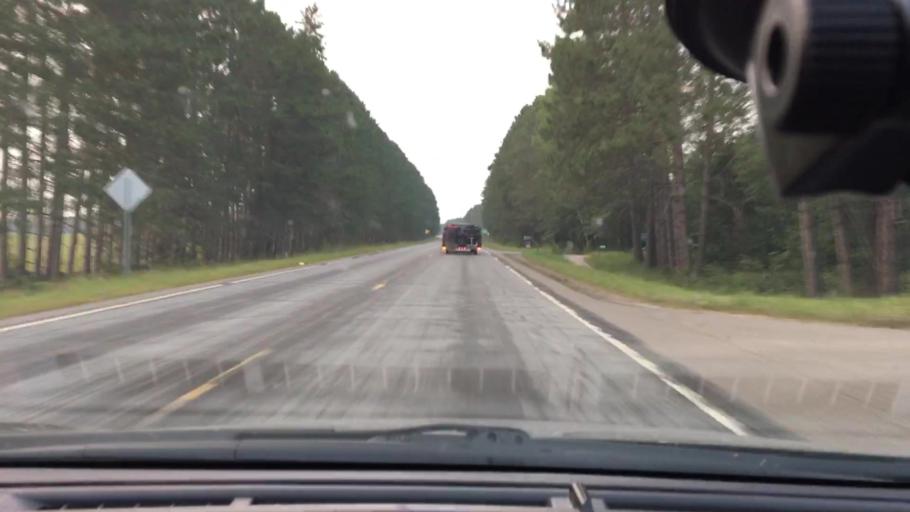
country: US
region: Minnesota
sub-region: Crow Wing County
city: Cross Lake
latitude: 46.7562
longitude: -93.9667
